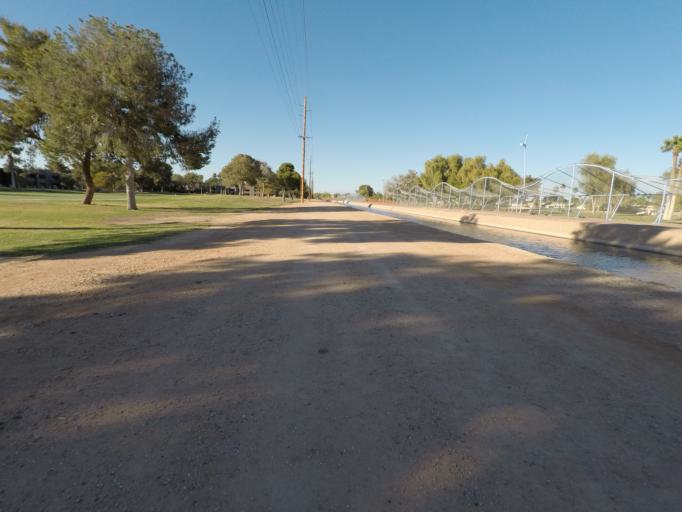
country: US
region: Arizona
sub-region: Maricopa County
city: Guadalupe
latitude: 33.3600
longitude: -111.9380
